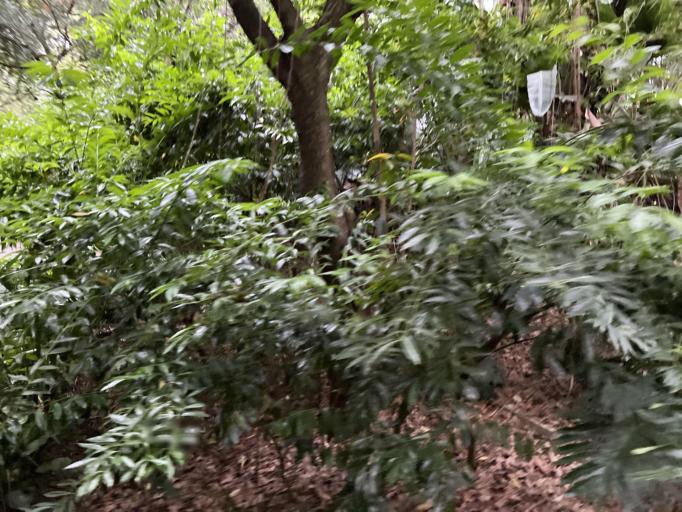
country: US
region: Florida
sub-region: Polk County
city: Citrus Ridge
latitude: 28.3619
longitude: -81.5924
